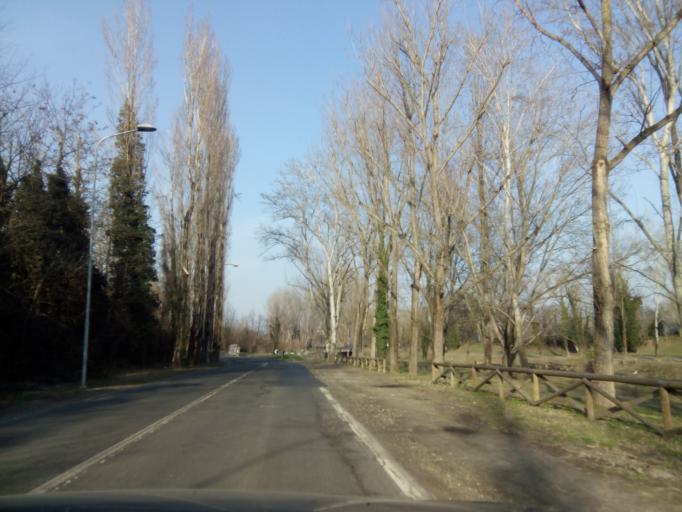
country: IT
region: Emilia-Romagna
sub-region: Provincia di Bologna
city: Imola
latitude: 44.3417
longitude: 11.7037
